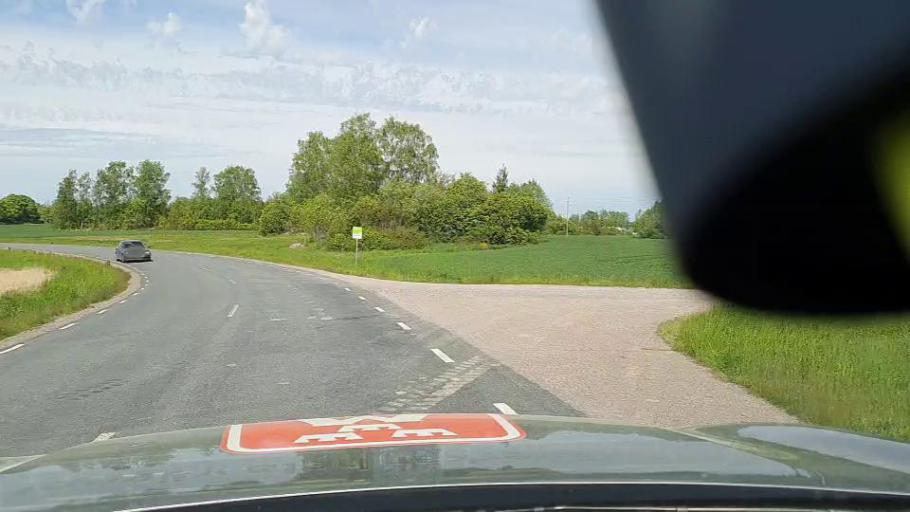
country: SE
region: Soedermanland
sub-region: Eskilstuna Kommun
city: Skogstorp
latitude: 59.3120
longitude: 16.4659
